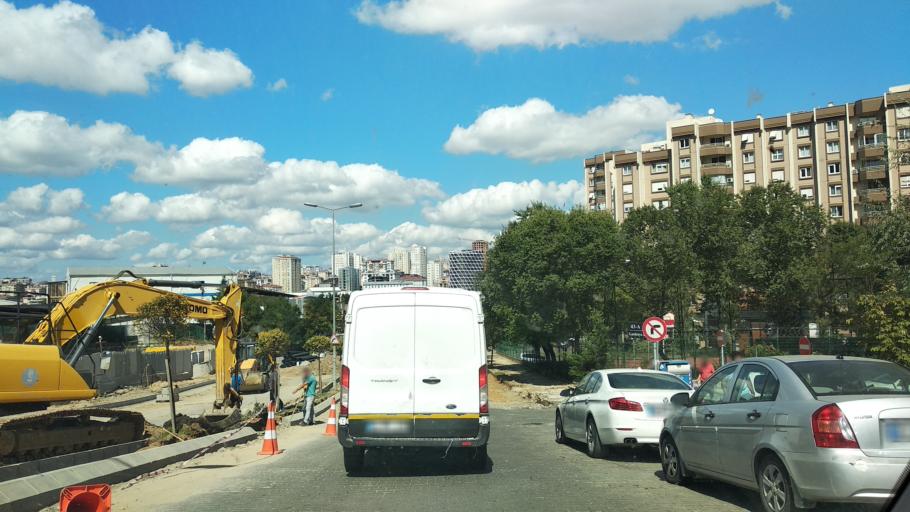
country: TR
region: Istanbul
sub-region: Atasehir
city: Atasehir
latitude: 40.9942
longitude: 29.1280
